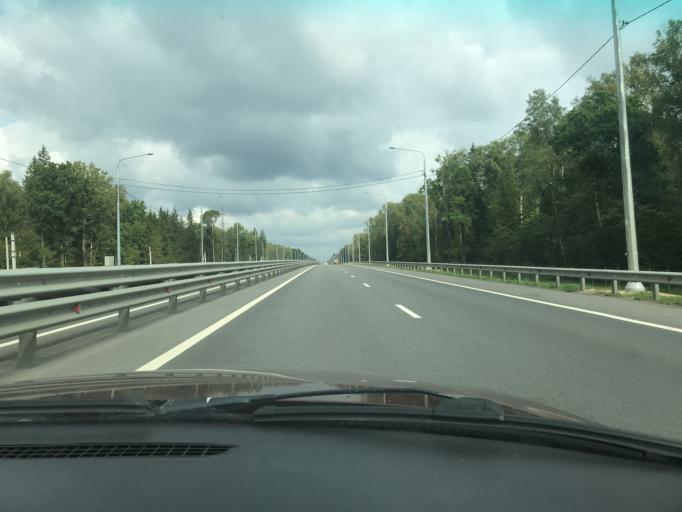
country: RU
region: Kaluga
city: Pyatovskiy
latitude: 54.6488
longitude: 36.1365
